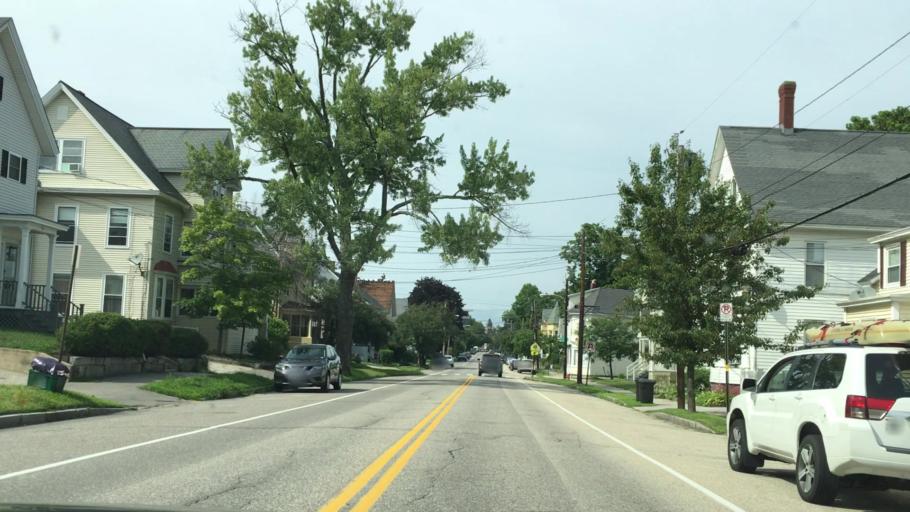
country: US
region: New Hampshire
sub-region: Merrimack County
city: Concord
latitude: 43.1976
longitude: -71.5392
